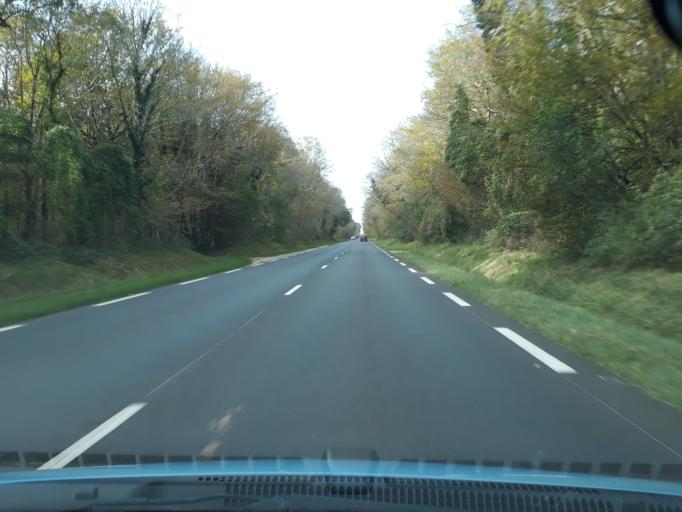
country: FR
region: Ile-de-France
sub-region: Departement de Seine-et-Marne
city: Acheres-la-Foret
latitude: 48.3592
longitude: 2.6242
